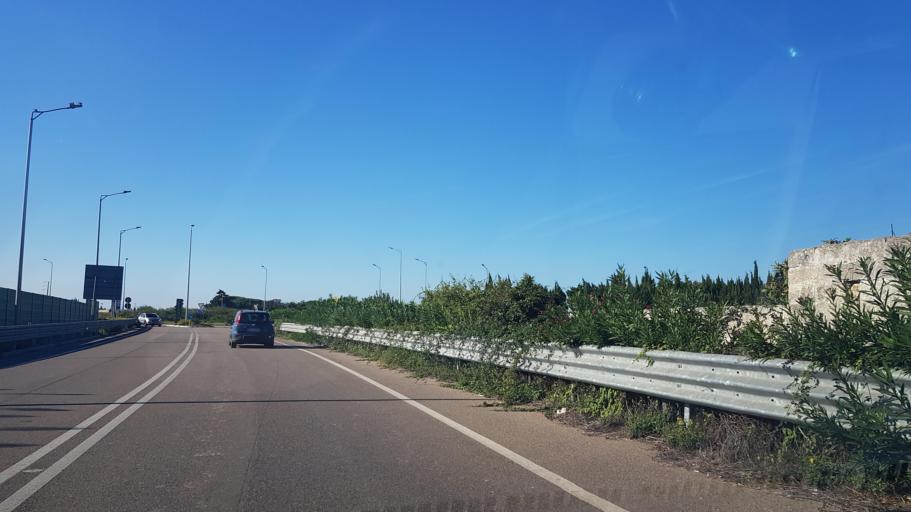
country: IT
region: Apulia
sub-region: Provincia di Lecce
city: Otranto
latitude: 40.1477
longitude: 18.4768
